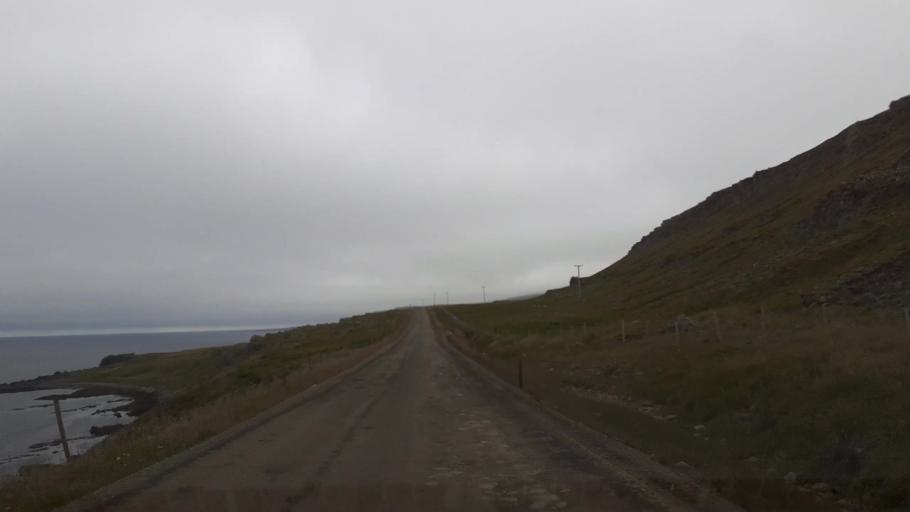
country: IS
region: Northwest
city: Saudarkrokur
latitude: 65.5184
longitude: -20.9691
